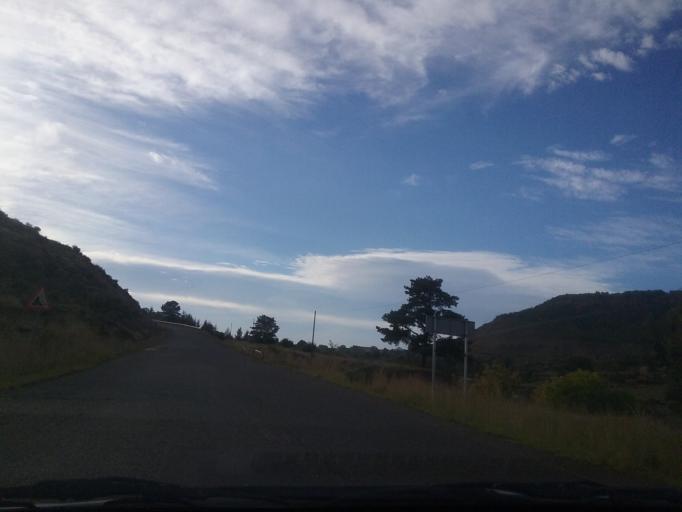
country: LS
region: Quthing
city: Quthing
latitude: -30.3891
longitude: 27.6103
